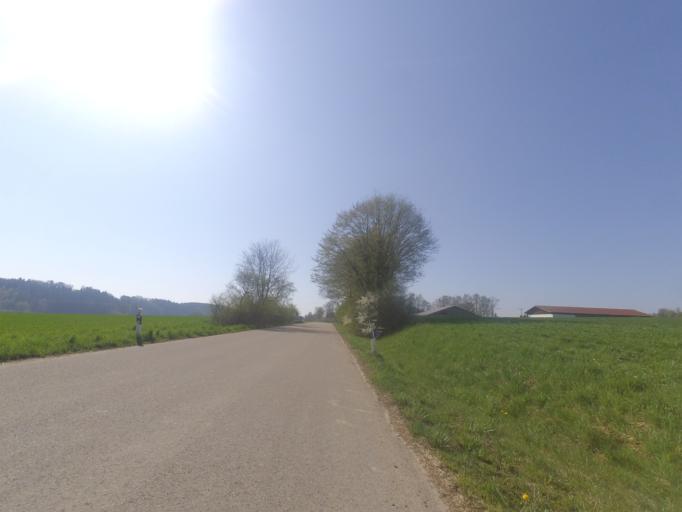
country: DE
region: Bavaria
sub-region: Swabia
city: Pfaffenhofen an der Roth
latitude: 48.3878
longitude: 10.1753
